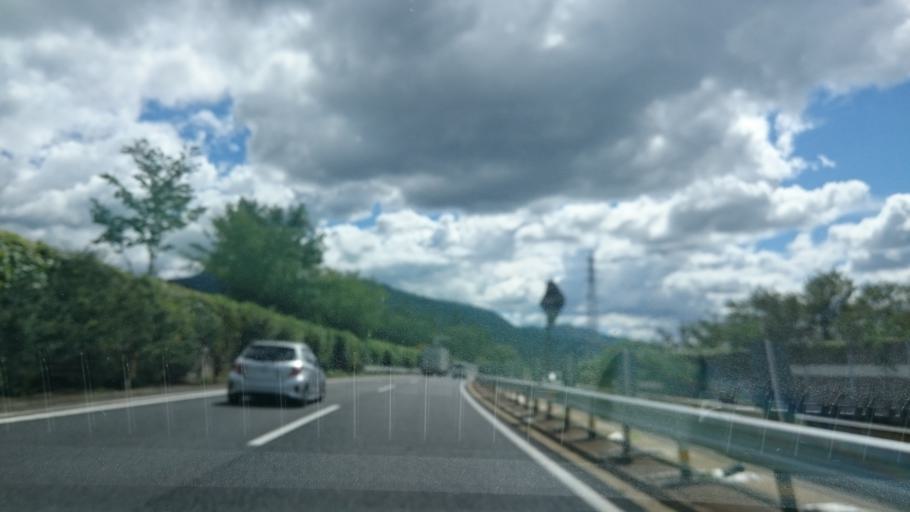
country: JP
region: Gifu
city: Nakatsugawa
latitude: 35.4881
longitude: 137.5141
